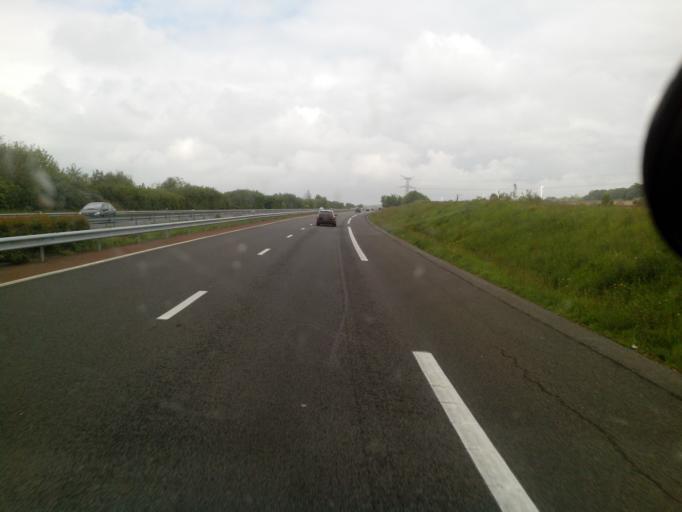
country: FR
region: Lower Normandy
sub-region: Departement de la Manche
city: Percy
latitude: 48.8853
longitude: -1.1422
